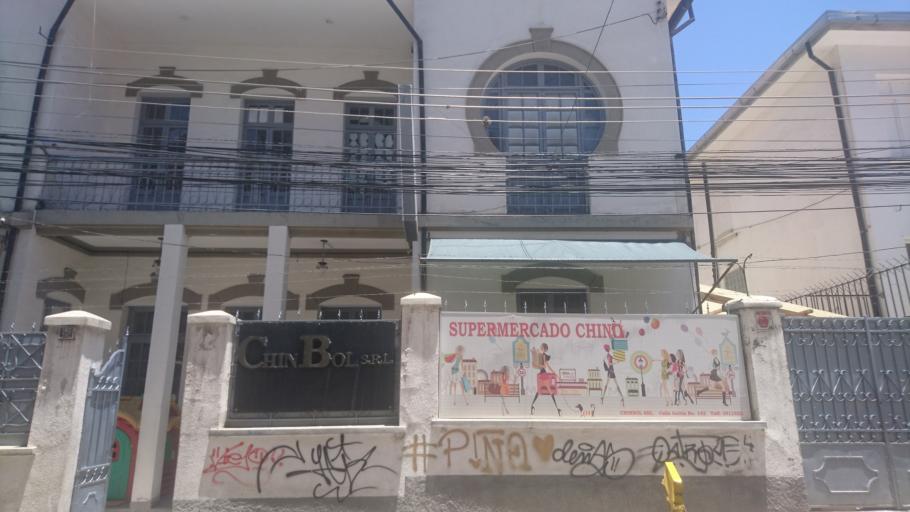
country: BO
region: La Paz
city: La Paz
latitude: -16.5052
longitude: -68.1289
